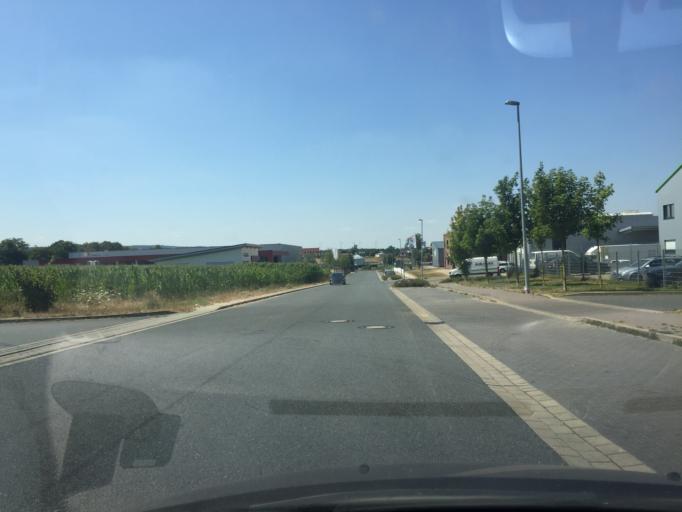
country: DE
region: Lower Saxony
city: Bockenem
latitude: 52.0024
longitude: 10.1451
